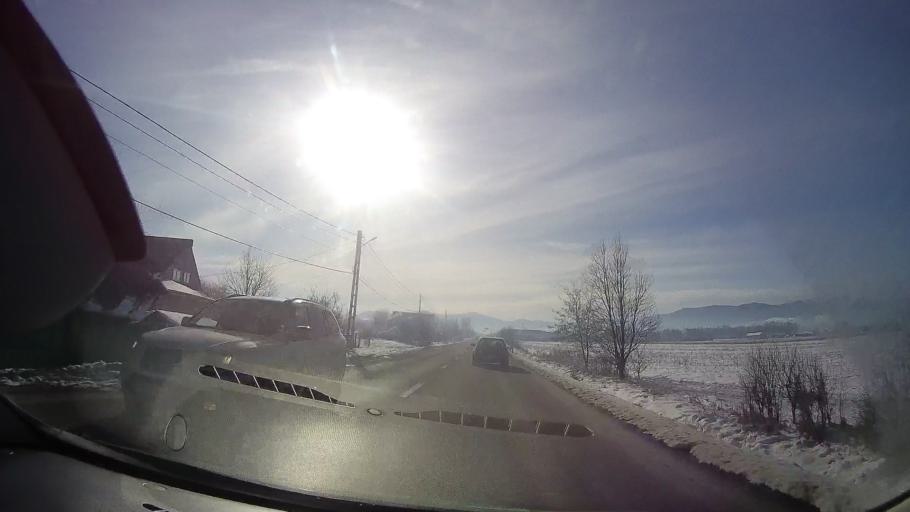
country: RO
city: Vanatori-Neamt
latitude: 47.1773
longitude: 26.3280
